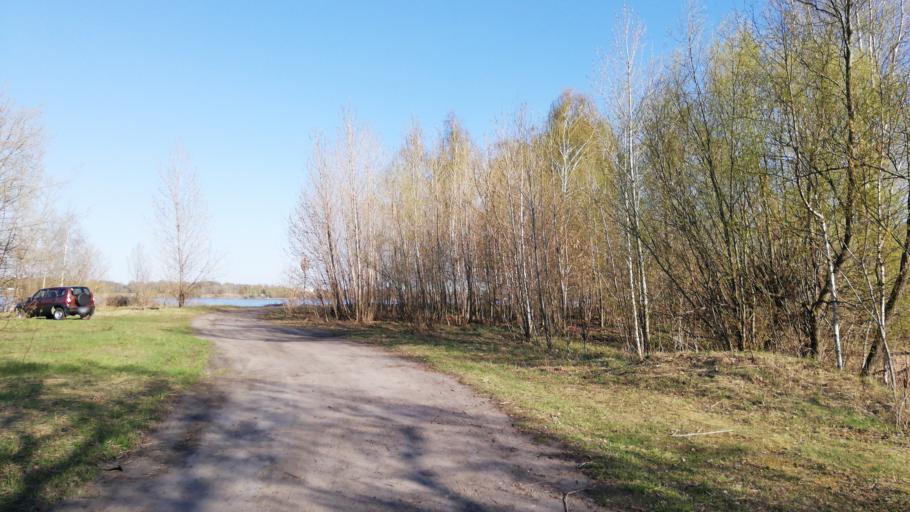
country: RU
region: Jaroslavl
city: Yaroslavl
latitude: 57.6139
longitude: 39.9051
